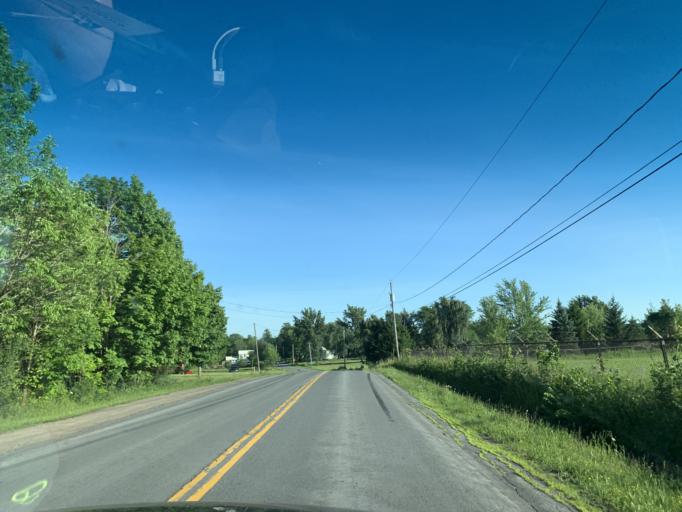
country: US
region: New York
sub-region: Oneida County
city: Vernon
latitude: 43.0595
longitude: -75.5082
